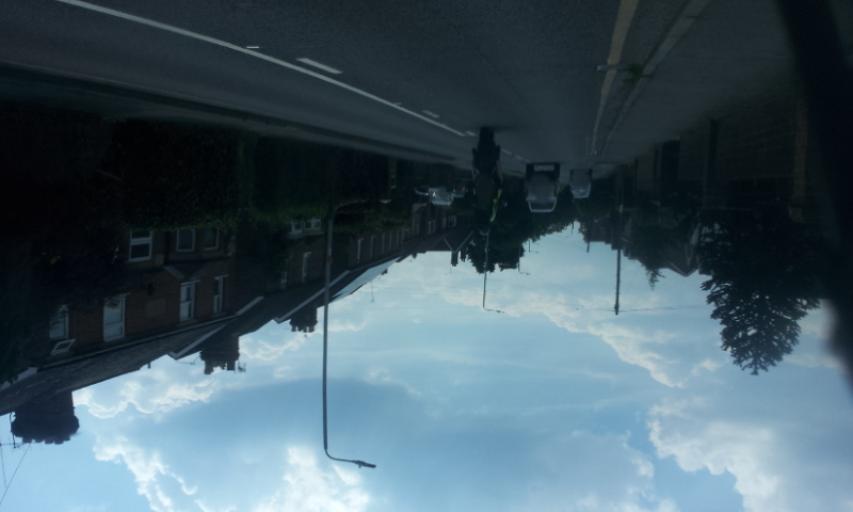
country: GB
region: England
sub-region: Kent
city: Paddock Wood
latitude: 51.1863
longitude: 0.3880
